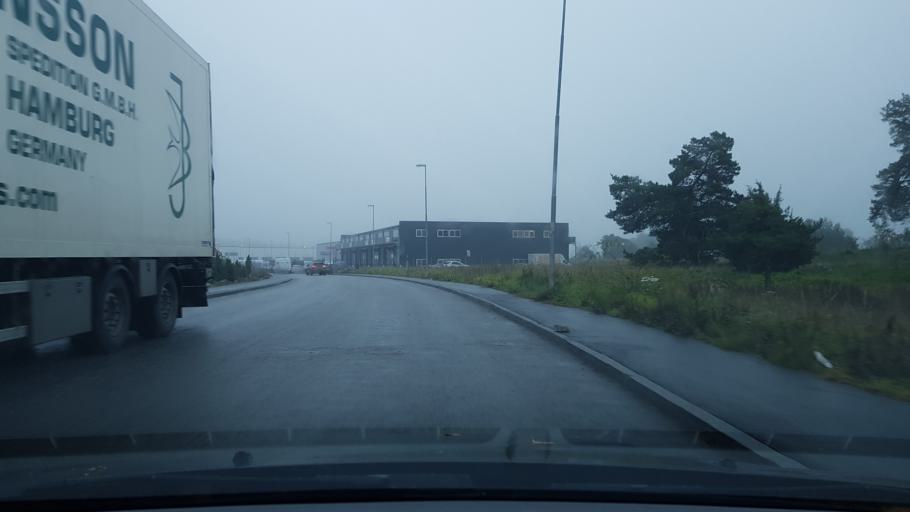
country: SE
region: Uppsala
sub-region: Uppsala Kommun
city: Saevja
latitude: 59.8411
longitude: 17.7233
